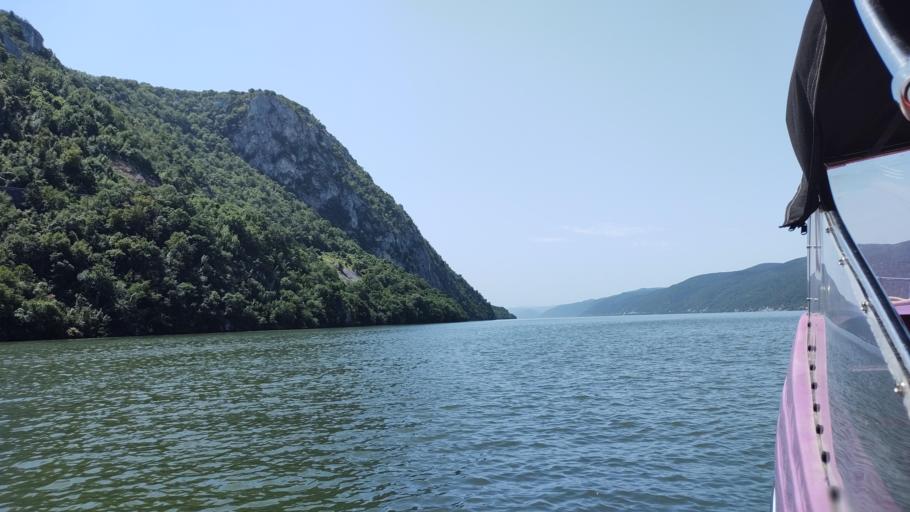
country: RO
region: Mehedinti
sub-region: Comuna Dubova
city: Dubova
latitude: 44.5889
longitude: 22.2576
